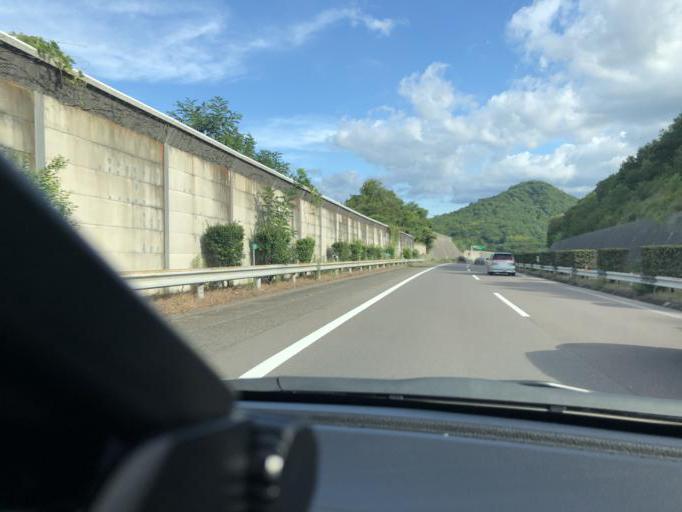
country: JP
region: Kagawa
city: Sakaidecho
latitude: 34.3176
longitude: 133.8374
